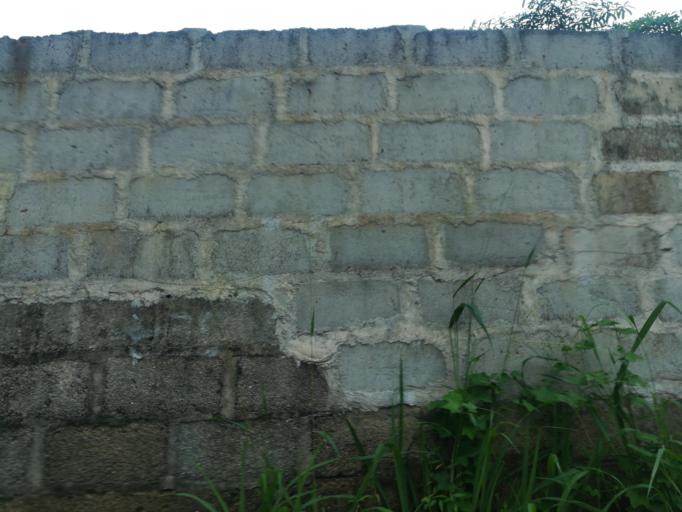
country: NG
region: Rivers
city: Port Harcourt
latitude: 4.7980
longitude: 6.9542
